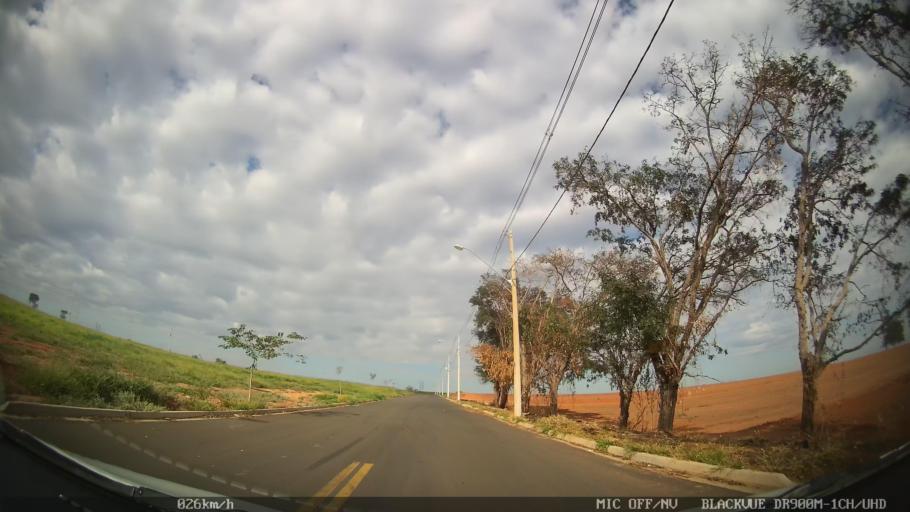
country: BR
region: Sao Paulo
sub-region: Santa Barbara D'Oeste
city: Santa Barbara d'Oeste
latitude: -22.7118
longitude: -47.3794
